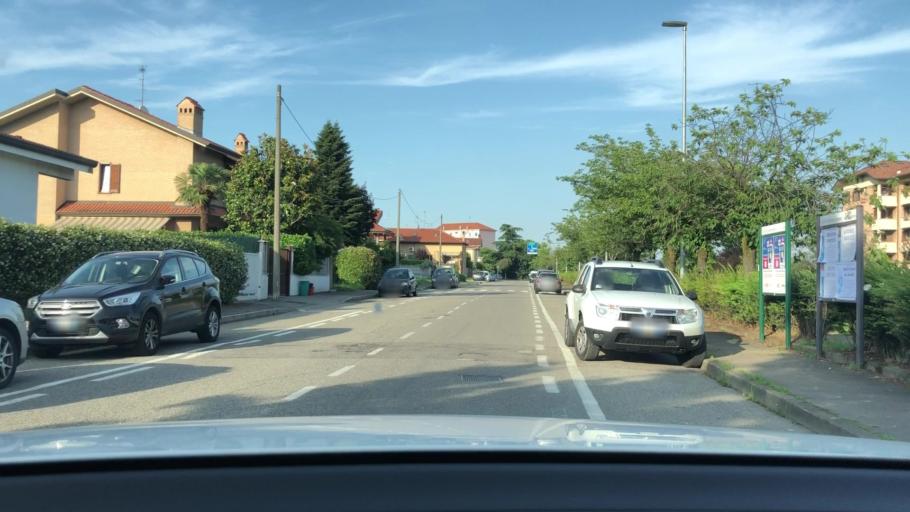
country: IT
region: Lombardy
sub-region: Citta metropolitana di Milano
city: Cusano Milanino
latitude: 45.5672
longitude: 9.1860
